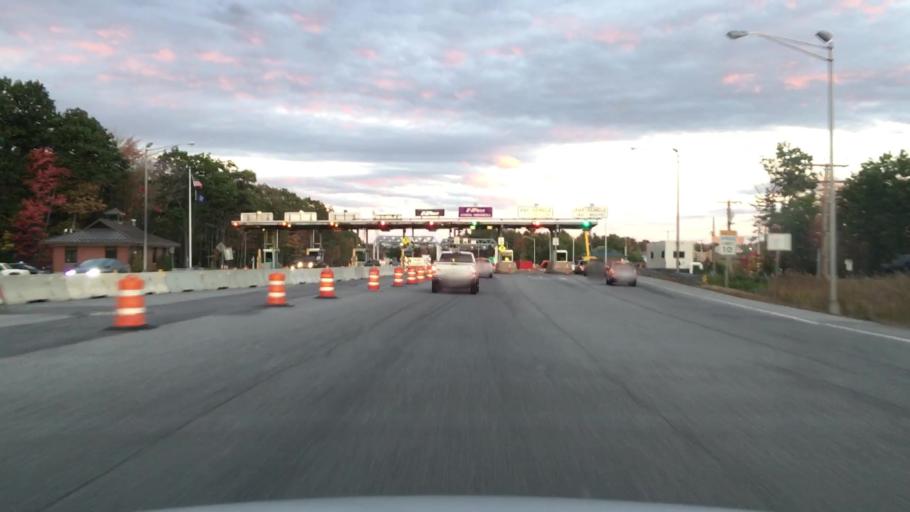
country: US
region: Maine
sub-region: Cumberland County
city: South Portland Gardens
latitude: 43.6258
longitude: -70.3438
